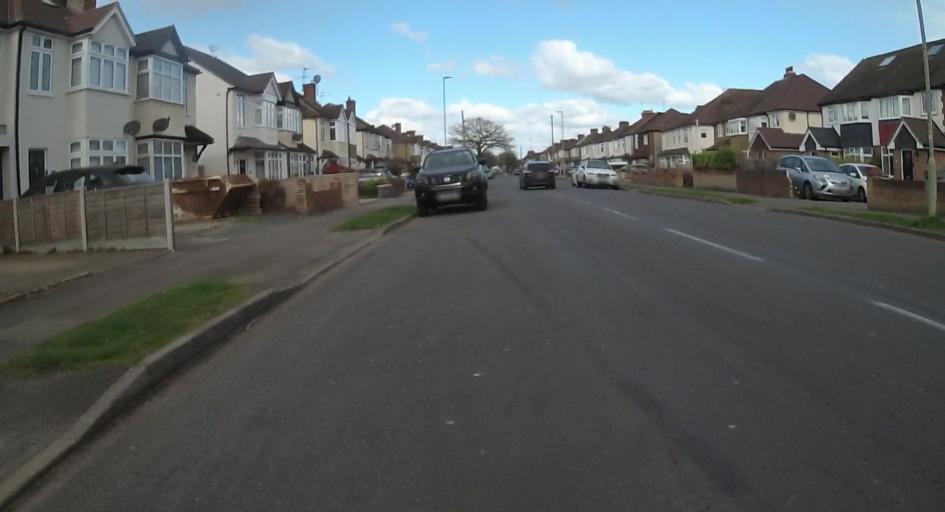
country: GB
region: England
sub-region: Surrey
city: West Byfleet
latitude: 51.3458
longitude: -0.5012
